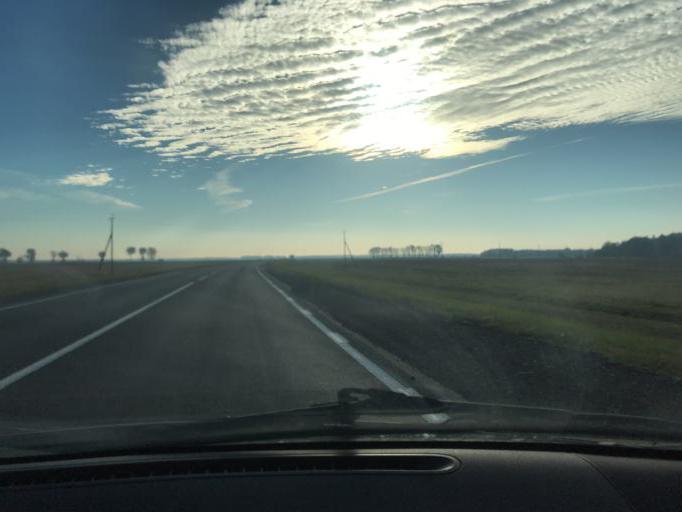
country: BY
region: Brest
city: Drahichyn
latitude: 52.2229
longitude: 25.1604
